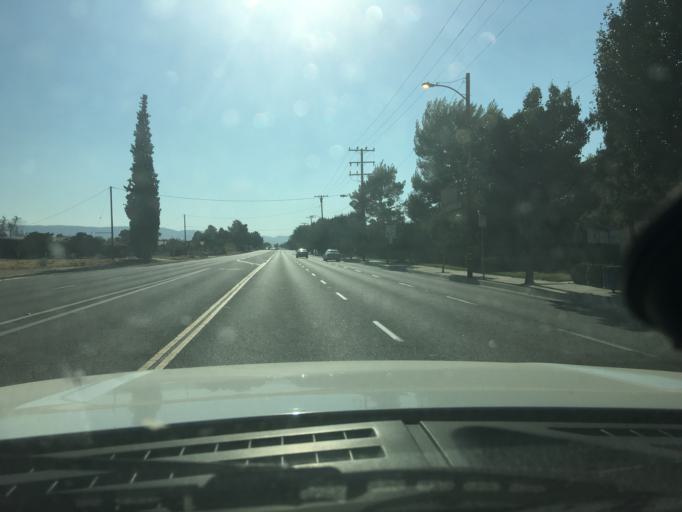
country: US
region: California
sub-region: Los Angeles County
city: Lancaster
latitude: 34.6604
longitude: -118.1568
